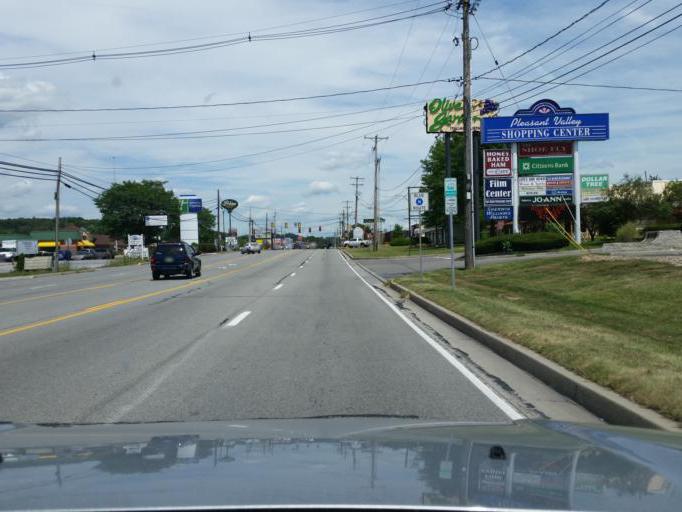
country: US
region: Pennsylvania
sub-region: Blair County
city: Lakemont
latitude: 40.4829
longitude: -78.4013
